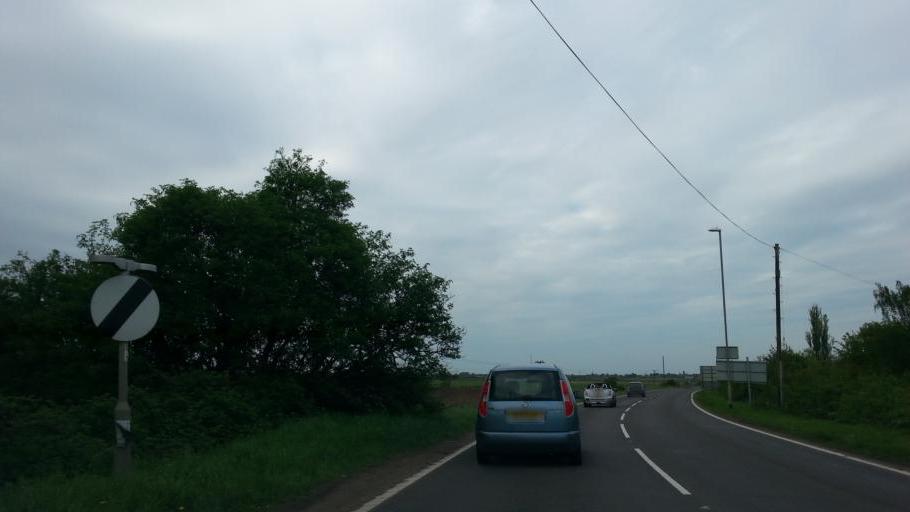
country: GB
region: England
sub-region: Cambridgeshire
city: Chatteris
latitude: 52.4653
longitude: 0.0439
